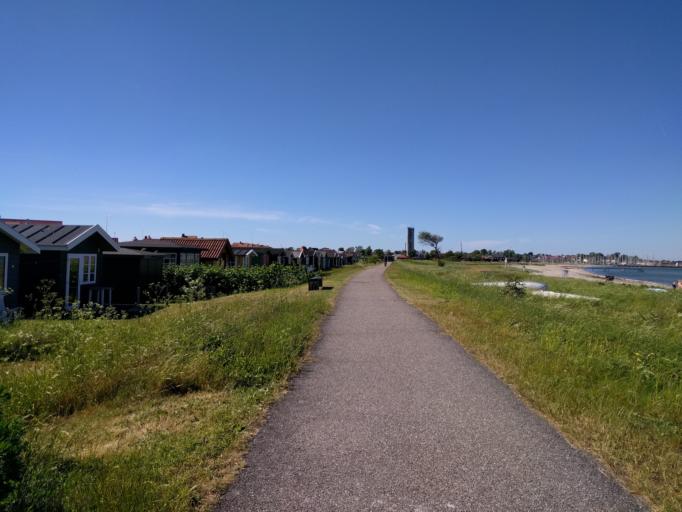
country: DK
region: South Denmark
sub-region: Kerteminde Kommune
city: Kerteminde
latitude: 55.4455
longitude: 10.6686
